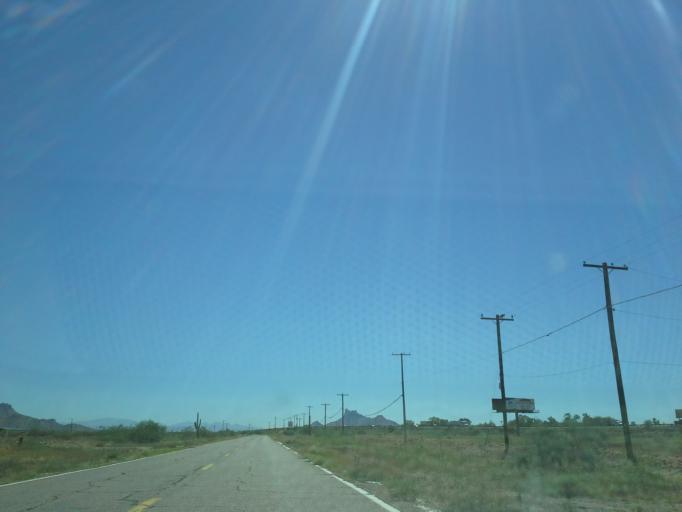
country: US
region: Arizona
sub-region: Pinal County
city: Eloy
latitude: 32.7174
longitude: -111.5036
